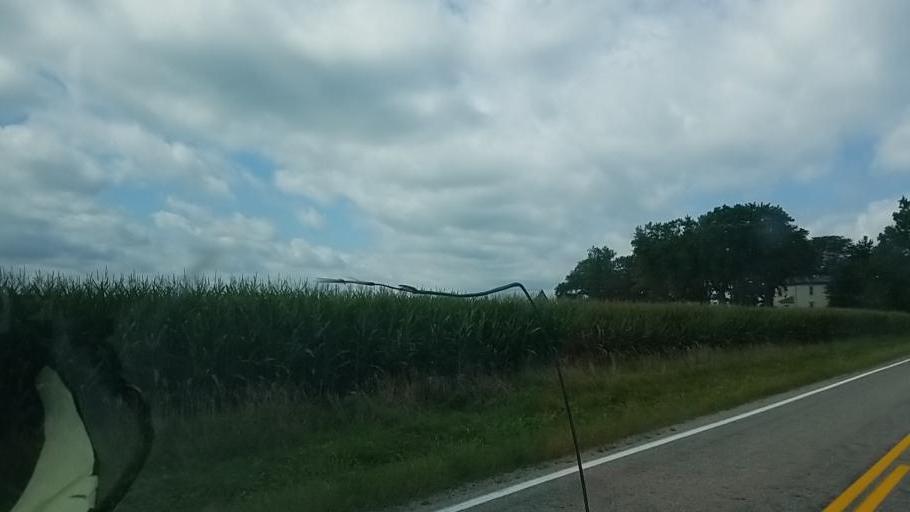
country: US
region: Ohio
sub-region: Madison County
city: Bethel
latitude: 39.7312
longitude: -83.3985
